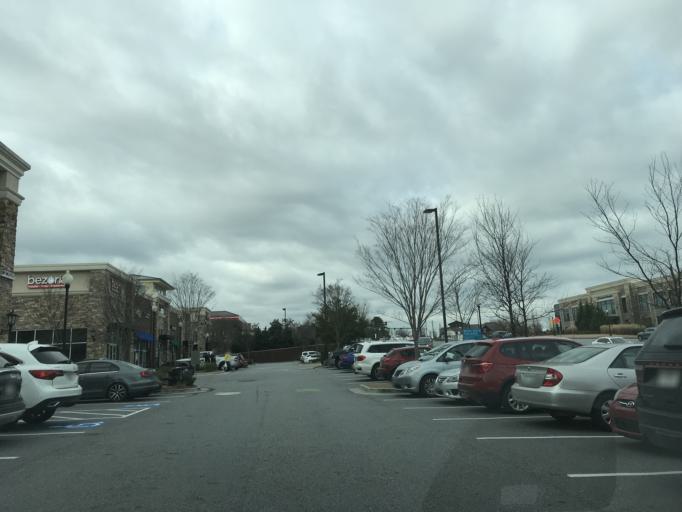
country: US
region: Georgia
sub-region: Fulton County
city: Alpharetta
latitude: 34.0686
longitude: -84.2806
